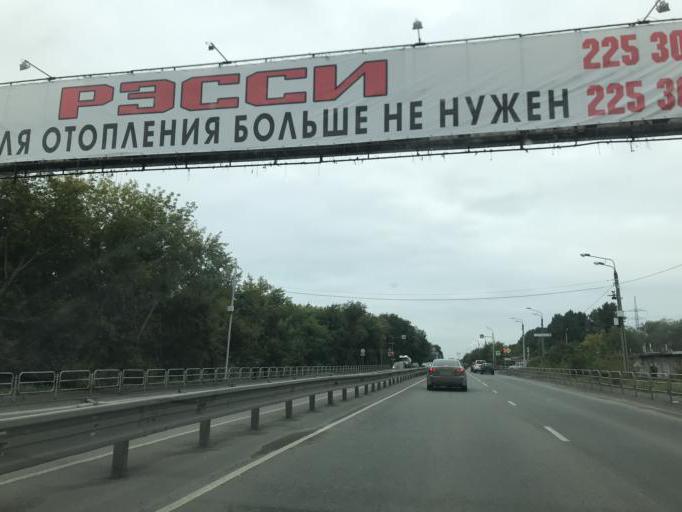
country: RU
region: Chelyabinsk
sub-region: Gorod Chelyabinsk
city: Chelyabinsk
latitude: 55.1785
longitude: 61.4207
